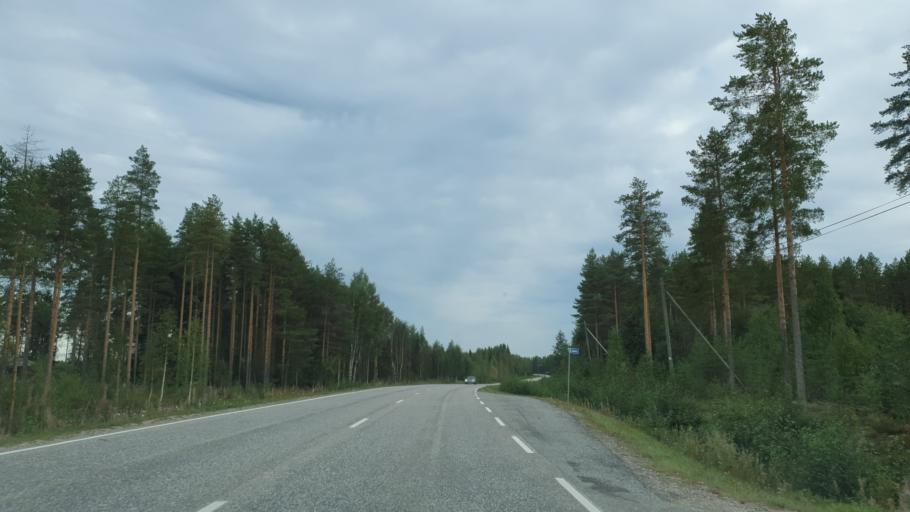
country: FI
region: Kainuu
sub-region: Kehys-Kainuu
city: Kuhmo
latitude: 64.1429
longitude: 29.4362
